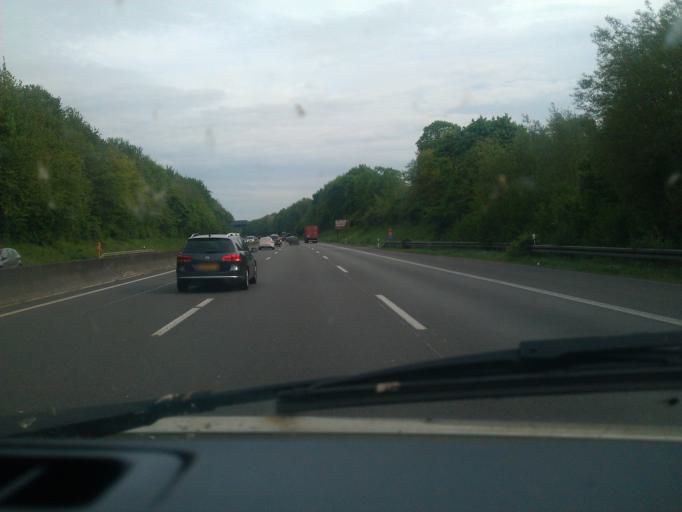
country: DE
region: North Rhine-Westphalia
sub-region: Regierungsbezirk Koln
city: Titz
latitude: 51.0721
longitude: 6.4290
